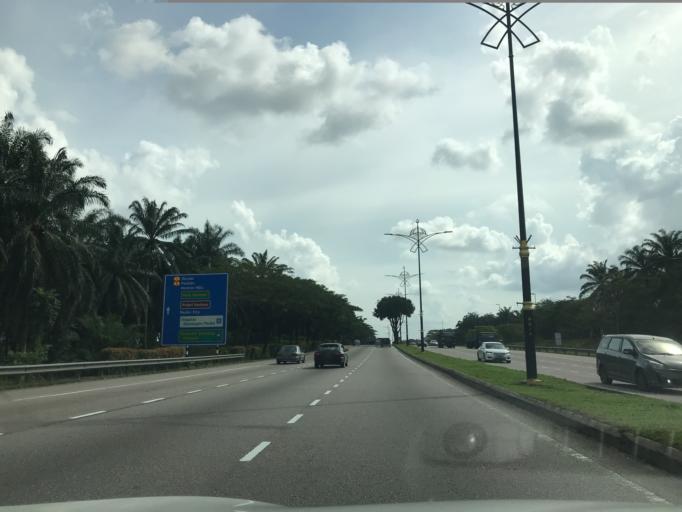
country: MY
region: Johor
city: Skudai
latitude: 1.5681
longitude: 103.6609
